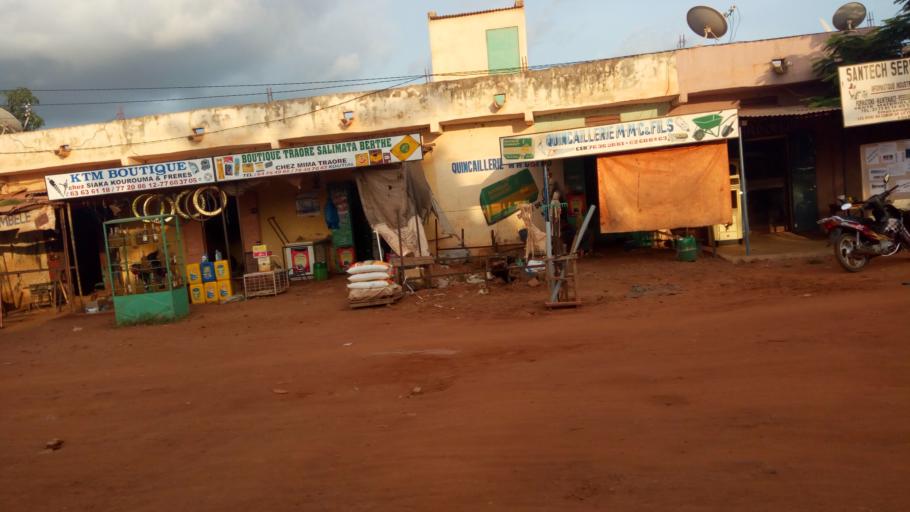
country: ML
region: Sikasso
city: Koutiala
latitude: 12.3774
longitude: -5.4731
